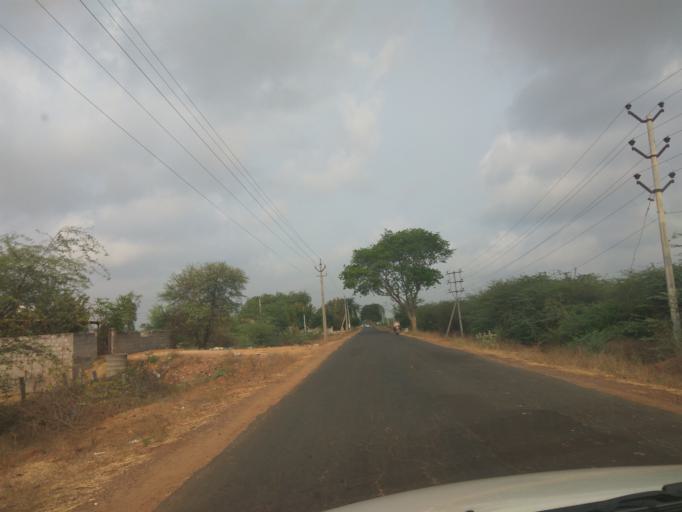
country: IN
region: Andhra Pradesh
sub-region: Prakasam
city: Kandukur
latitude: 15.2092
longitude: 79.8902
